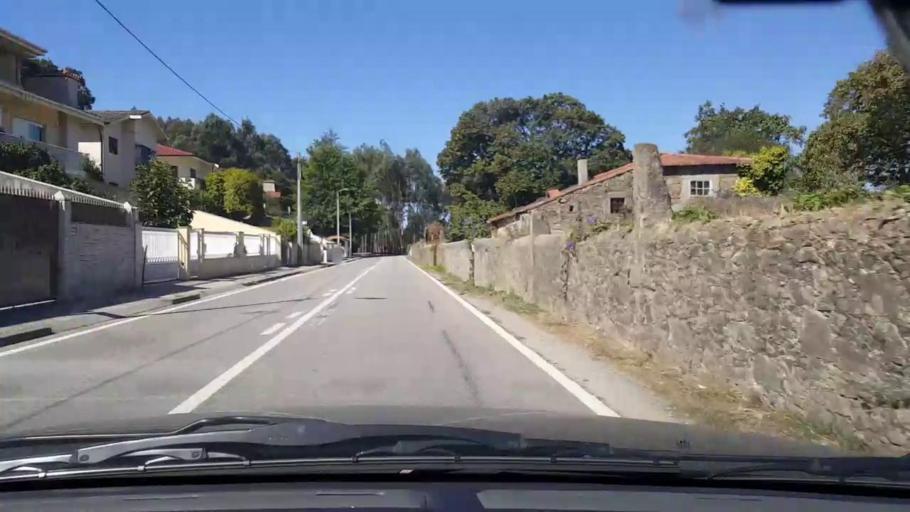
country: PT
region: Porto
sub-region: Vila do Conde
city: Arvore
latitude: 41.3398
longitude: -8.6473
